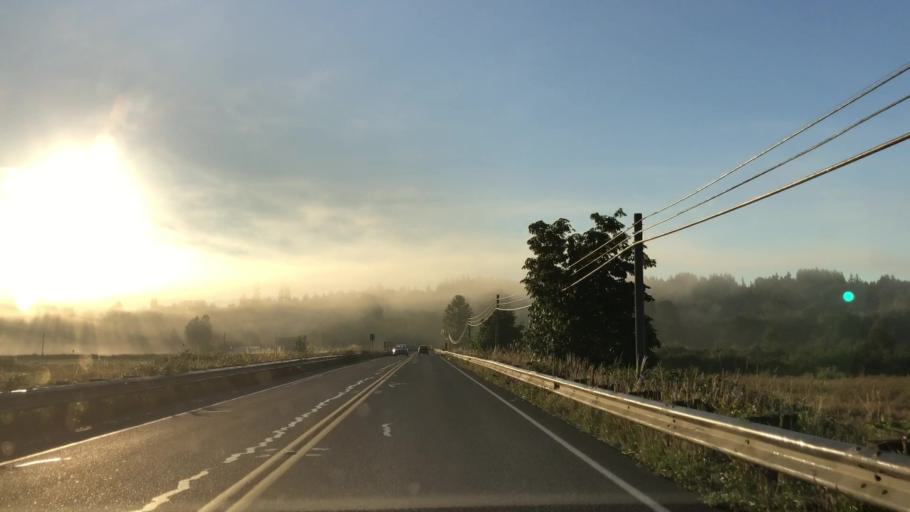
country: US
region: Washington
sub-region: King County
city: Duvall
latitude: 47.7438
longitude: -121.9960
